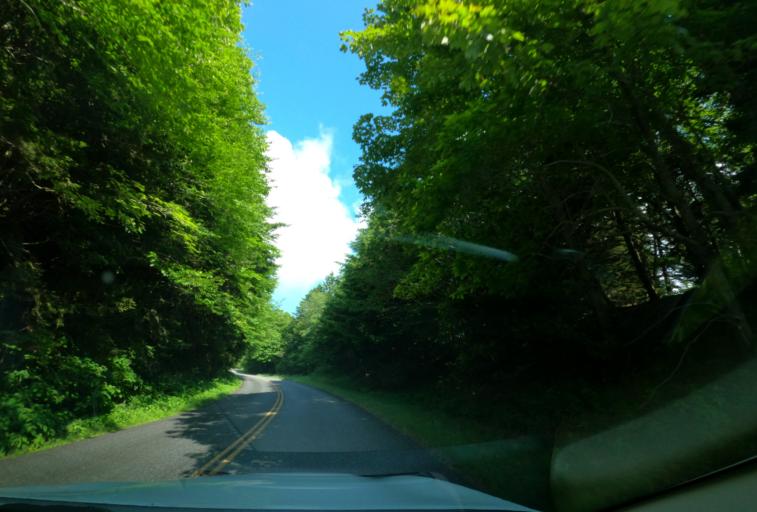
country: US
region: North Carolina
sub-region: Haywood County
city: Hazelwood
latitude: 35.3170
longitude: -82.9545
